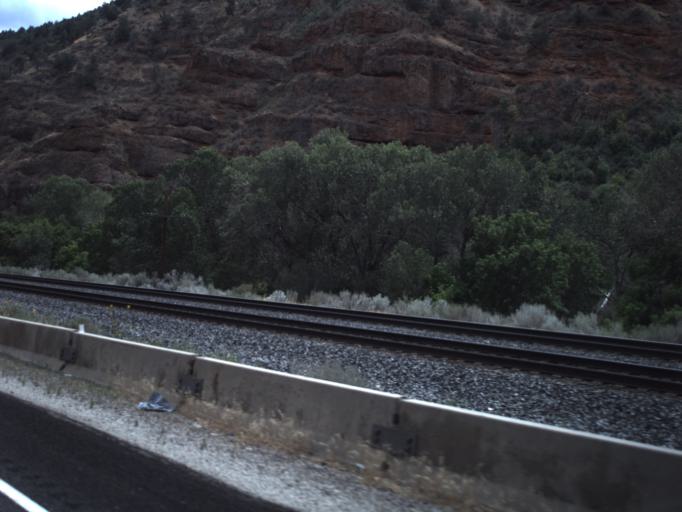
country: US
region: Utah
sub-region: Utah County
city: Mapleton
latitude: 39.9941
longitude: -111.4009
